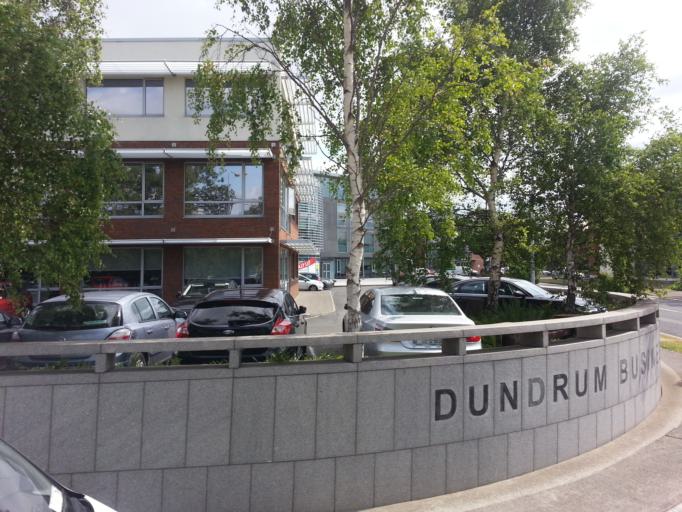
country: IE
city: Milltown
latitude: 53.3030
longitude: -6.2451
